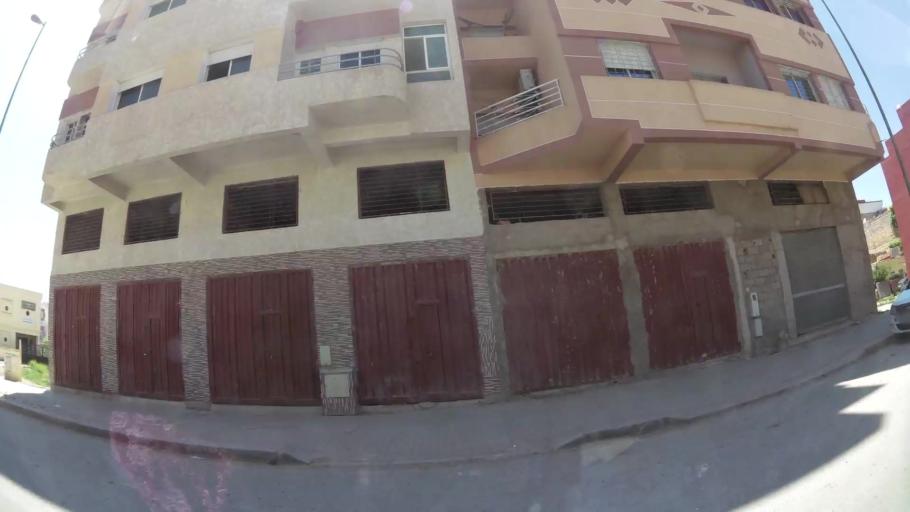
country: MA
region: Fes-Boulemane
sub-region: Fes
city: Fes
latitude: 34.0306
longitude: -5.0433
